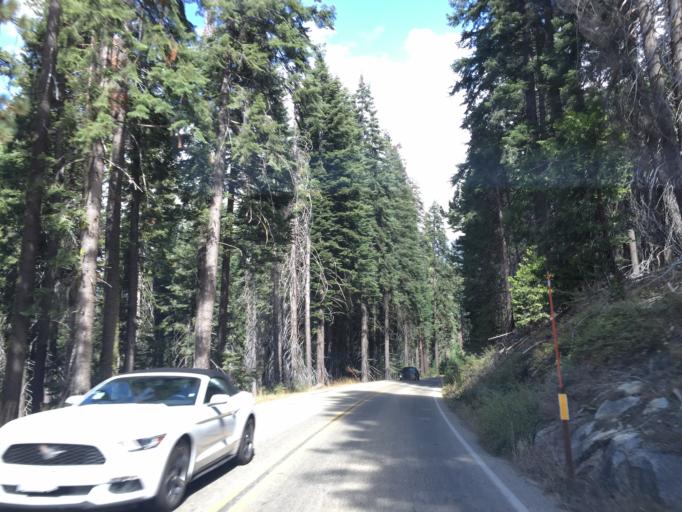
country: US
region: California
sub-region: Tulare County
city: Three Rivers
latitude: 36.5932
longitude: -118.7508
